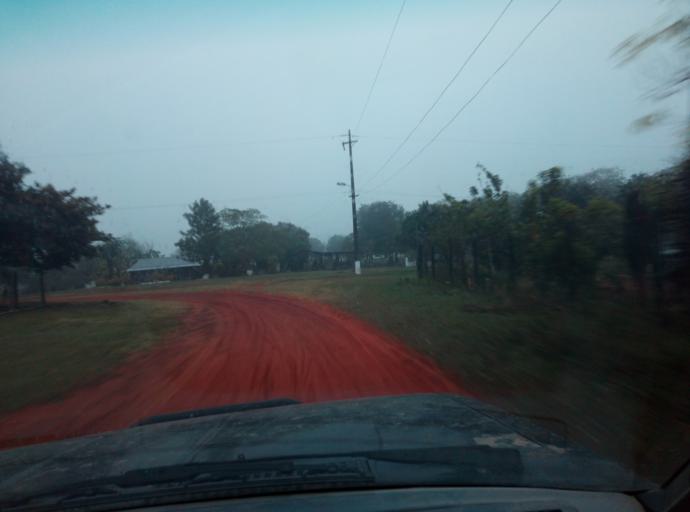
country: PY
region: Caaguazu
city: Doctor Cecilio Baez
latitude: -25.1545
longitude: -56.2909
